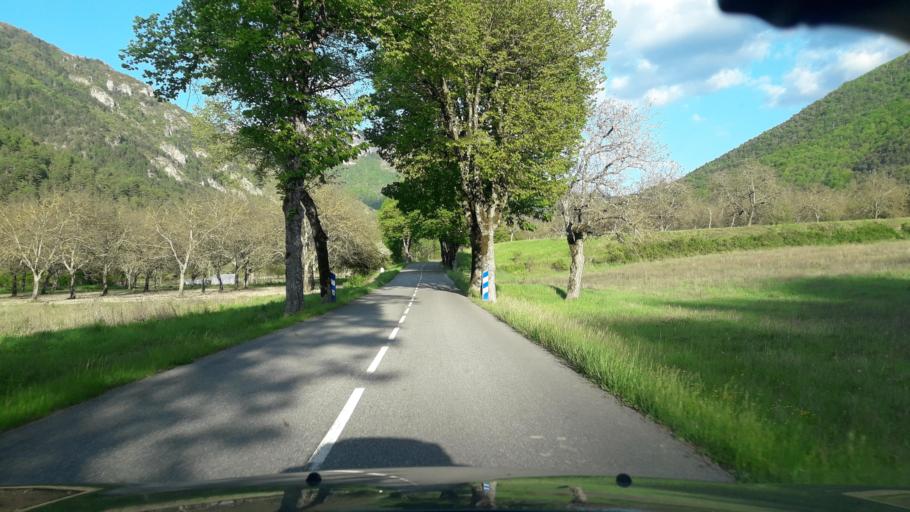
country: FR
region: Rhone-Alpes
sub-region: Departement de la Drome
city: Die
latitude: 44.6918
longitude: 5.4924
